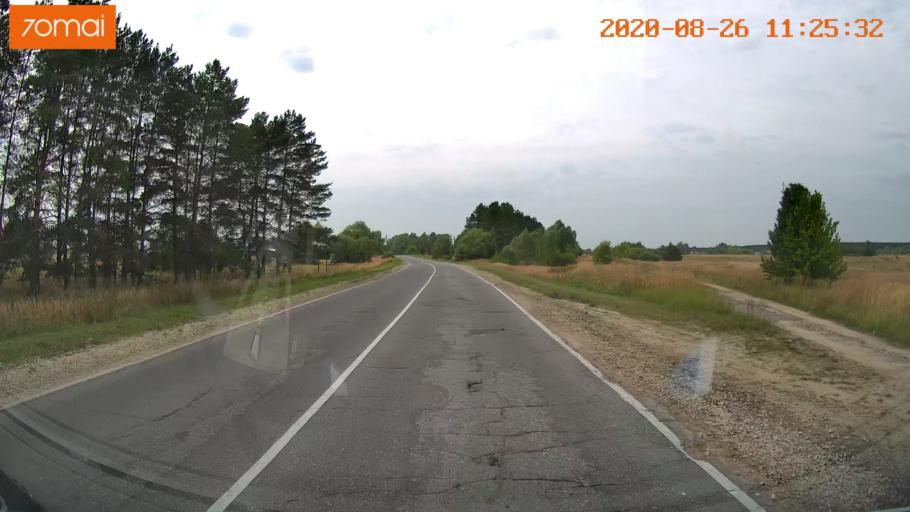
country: RU
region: Rjazan
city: Shilovo
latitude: 54.3413
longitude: 40.9627
